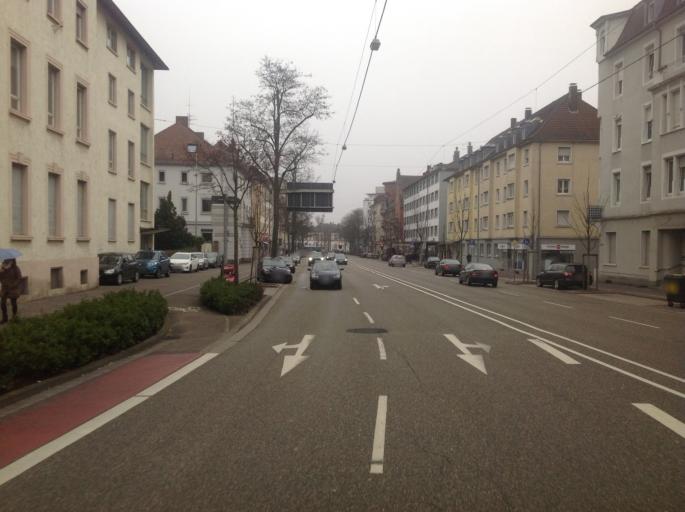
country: DE
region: Baden-Wuerttemberg
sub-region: Karlsruhe Region
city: Rastatt
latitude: 48.8593
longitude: 8.2111
